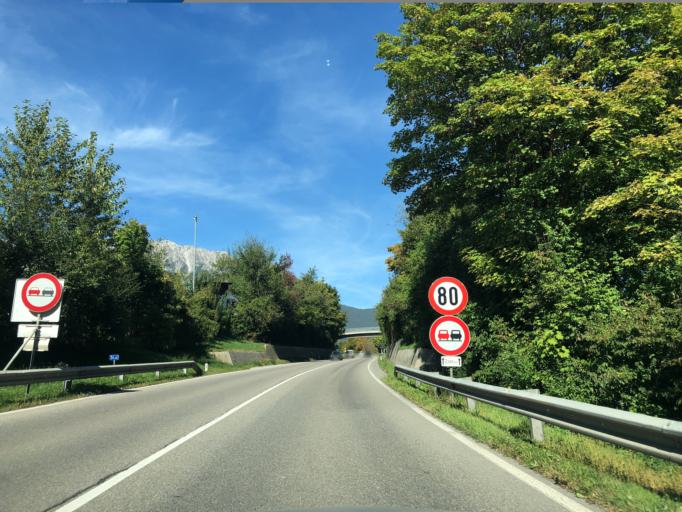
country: AT
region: Tyrol
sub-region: Politischer Bezirk Imst
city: Imst
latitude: 47.2429
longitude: 10.7436
